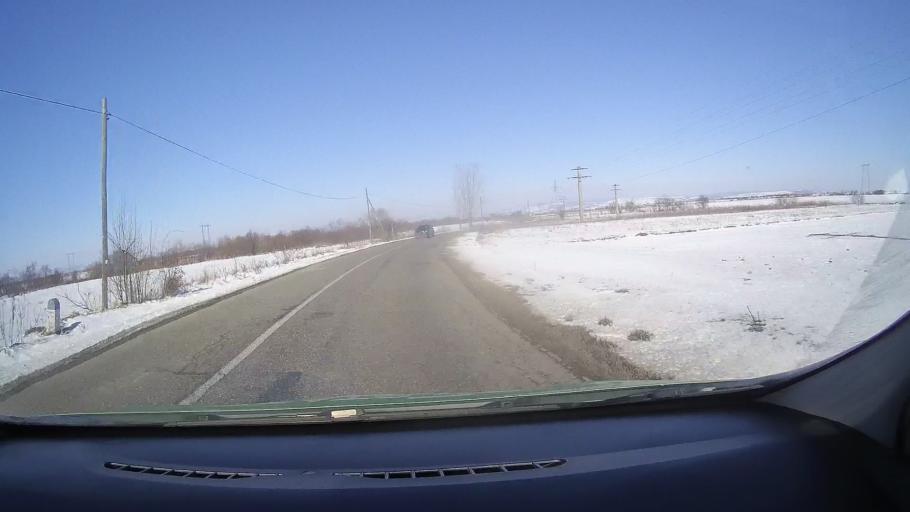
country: RO
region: Brasov
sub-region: Comuna Harseni
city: Harseni
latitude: 45.7717
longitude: 25.0013
